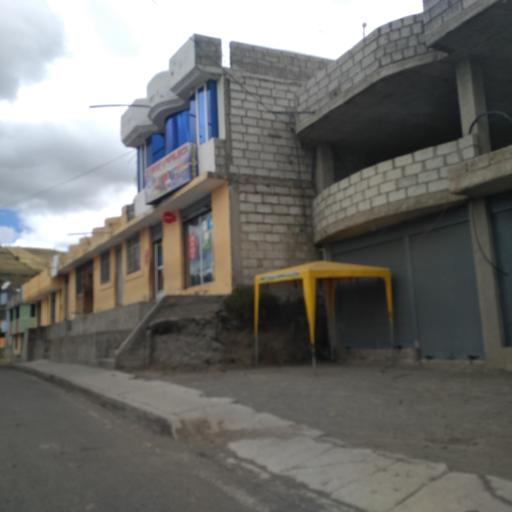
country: EC
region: Cotopaxi
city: Saquisili
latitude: -0.7484
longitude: -78.7219
